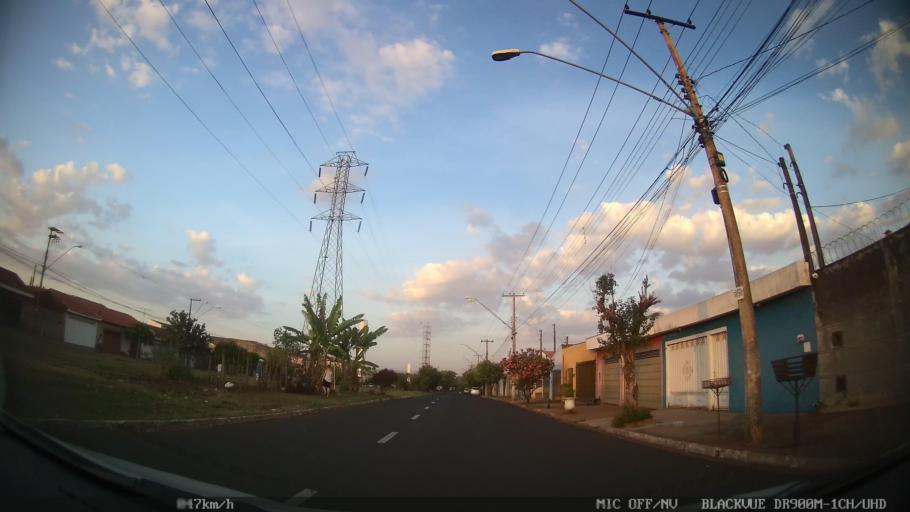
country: BR
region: Sao Paulo
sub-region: Ribeirao Preto
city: Ribeirao Preto
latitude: -21.1199
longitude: -47.8193
